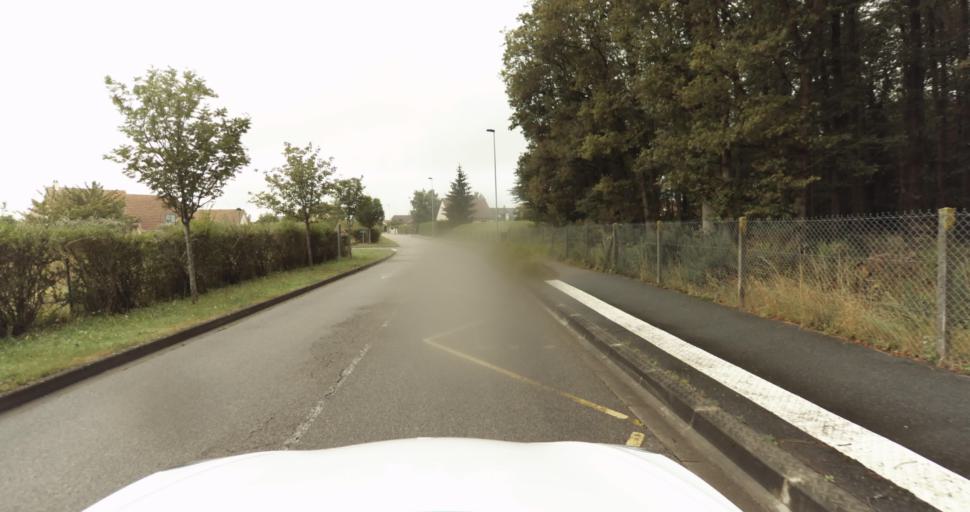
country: FR
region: Haute-Normandie
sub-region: Departement de l'Eure
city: Evreux
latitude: 49.0403
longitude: 1.1372
